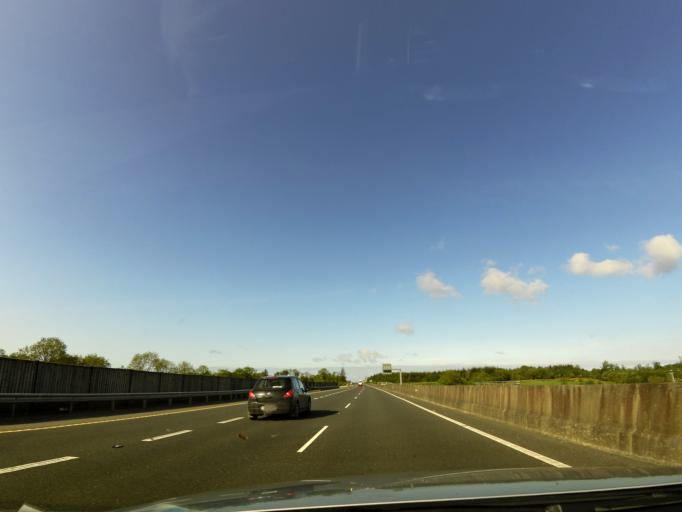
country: IE
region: Munster
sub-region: North Tipperary
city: Newport
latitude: 52.7545
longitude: -8.4151
